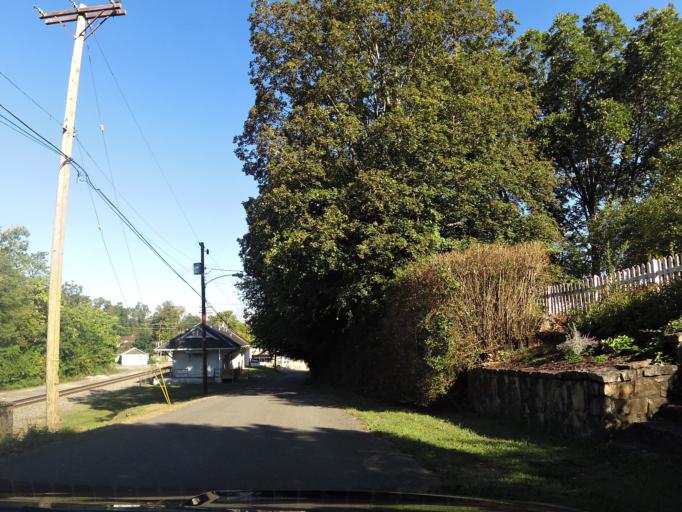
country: US
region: Kentucky
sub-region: Whitley County
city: Williamsburg
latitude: 36.7397
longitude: -84.1614
